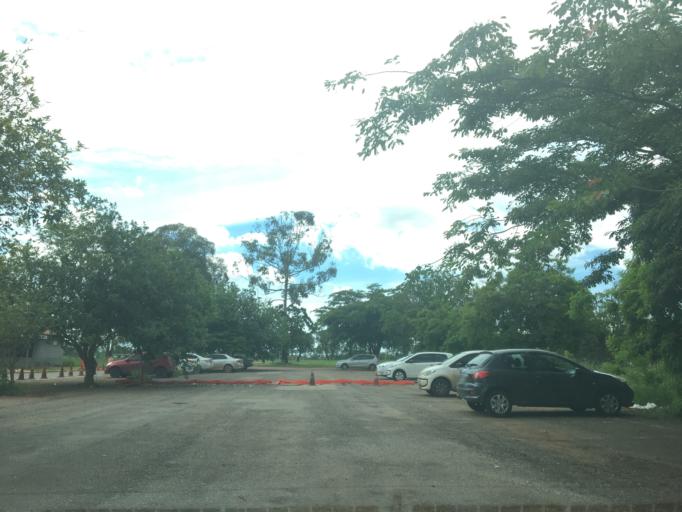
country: BR
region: Federal District
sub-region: Brasilia
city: Brasilia
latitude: -15.8255
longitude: -47.9408
